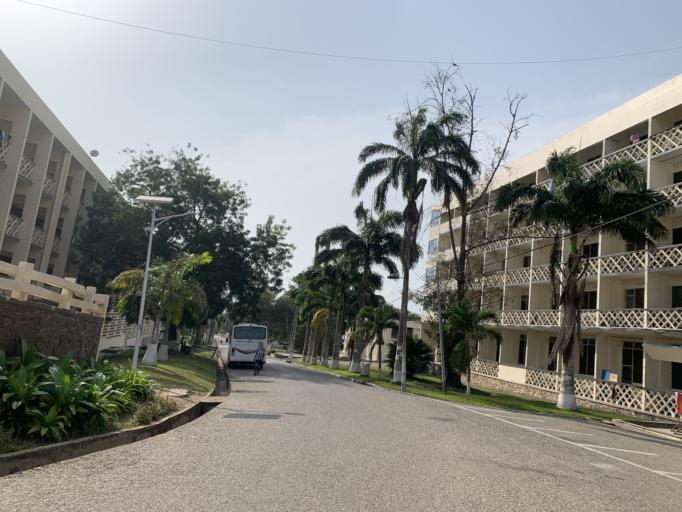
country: GH
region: Central
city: Winneba
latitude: 5.3390
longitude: -0.6251
